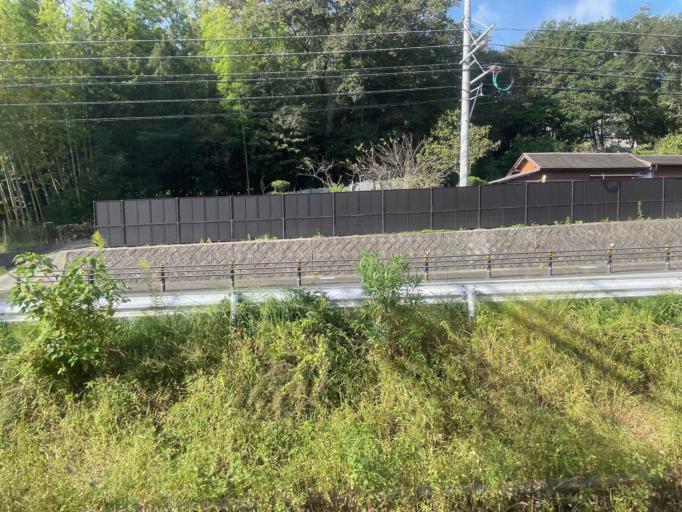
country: JP
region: Mie
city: Toba
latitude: 34.3987
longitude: 136.8138
